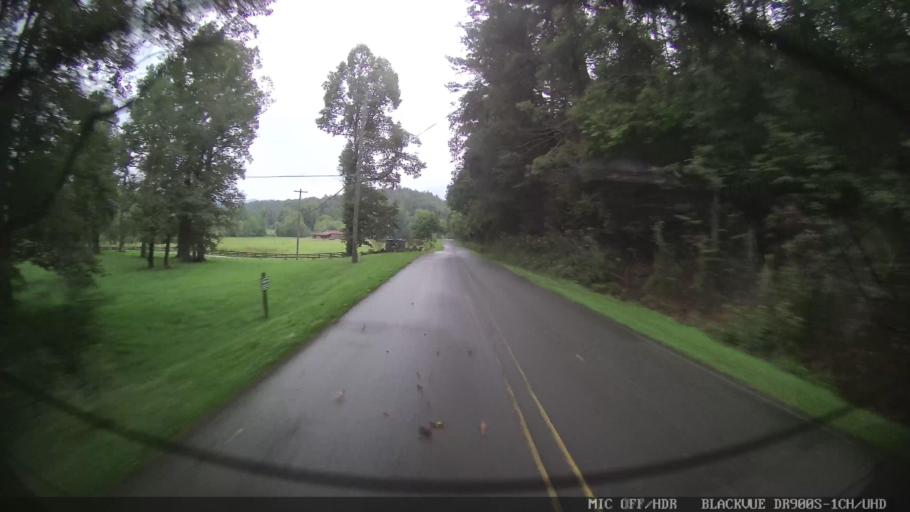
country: US
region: Georgia
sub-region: Gilmer County
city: Ellijay
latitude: 34.7606
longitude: -84.5315
